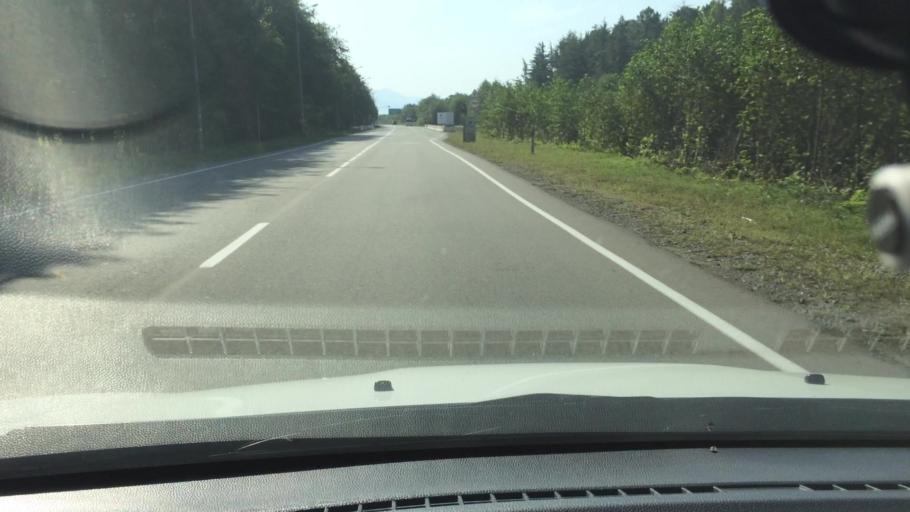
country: GE
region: Guria
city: Urek'i
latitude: 41.9454
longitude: 41.7706
